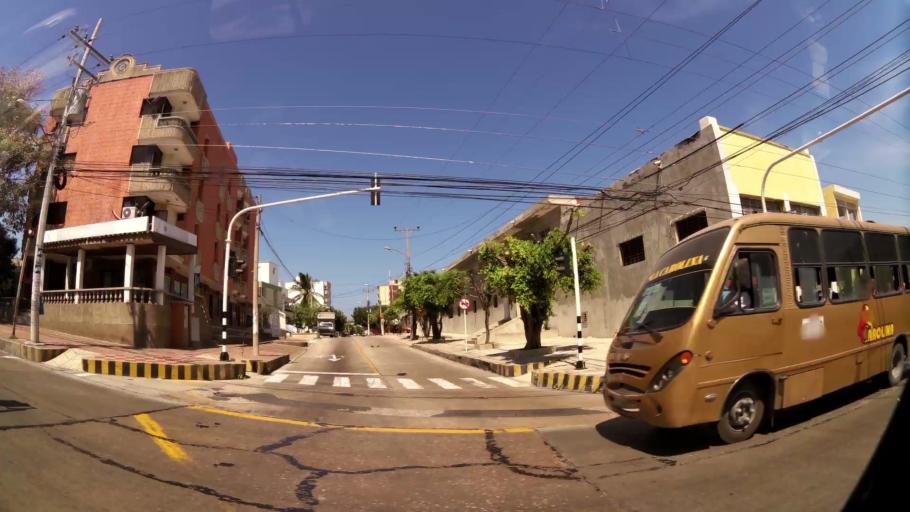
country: CO
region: Atlantico
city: Barranquilla
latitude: 10.9833
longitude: -74.8034
